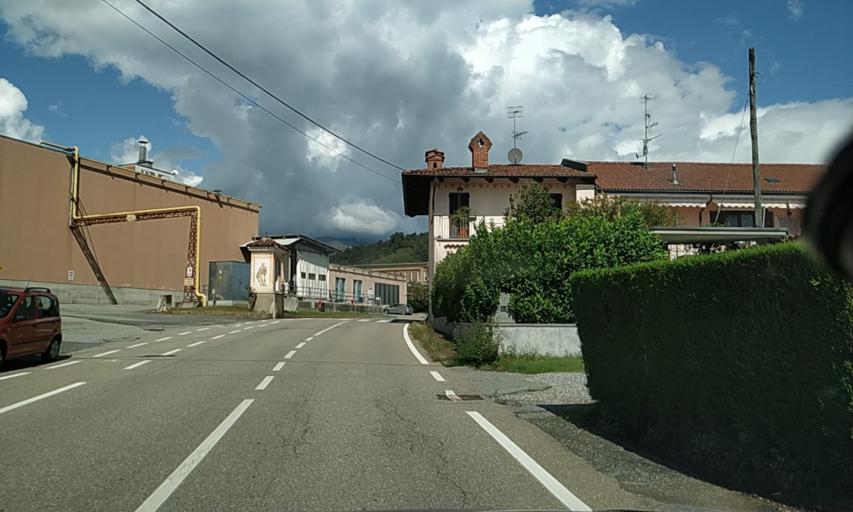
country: IT
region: Piedmont
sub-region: Provincia di Biella
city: Ceresane-Curanuova
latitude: 45.5251
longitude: 8.0050
